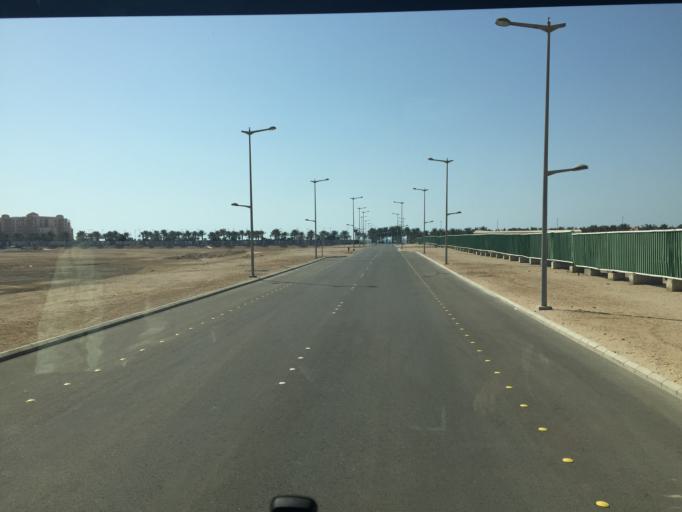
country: SA
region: Makkah
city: Rabigh
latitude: 22.4114
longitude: 39.0818
